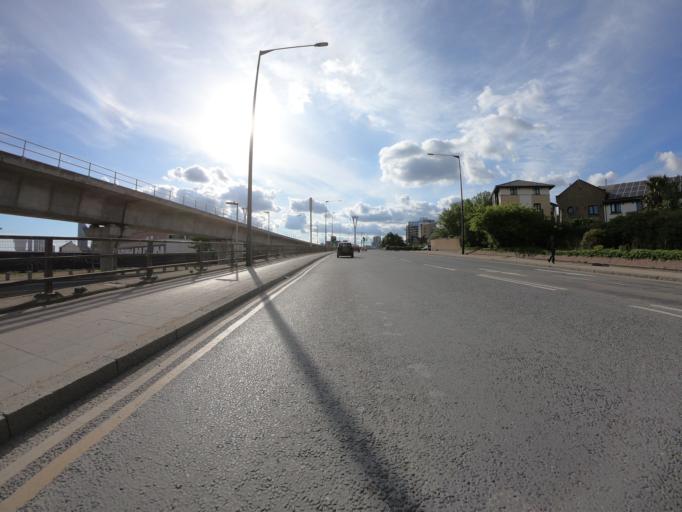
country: GB
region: England
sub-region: Greater London
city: Poplar
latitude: 51.5036
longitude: 0.0211
